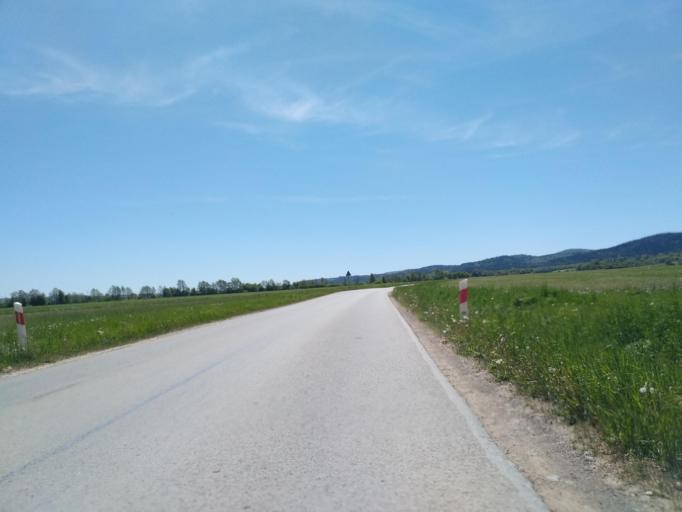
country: PL
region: Subcarpathian Voivodeship
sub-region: Powiat krosnienski
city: Sieniawa
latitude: 49.5381
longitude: 21.9707
